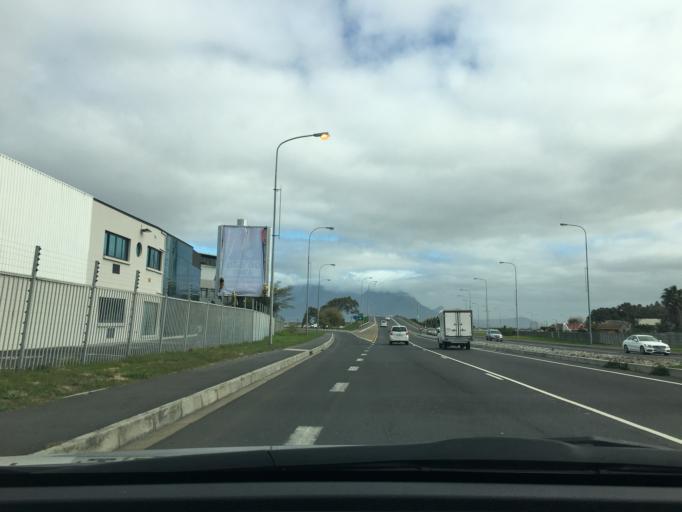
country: ZA
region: Western Cape
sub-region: City of Cape Town
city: Lansdowne
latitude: -33.9679
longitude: 18.5775
